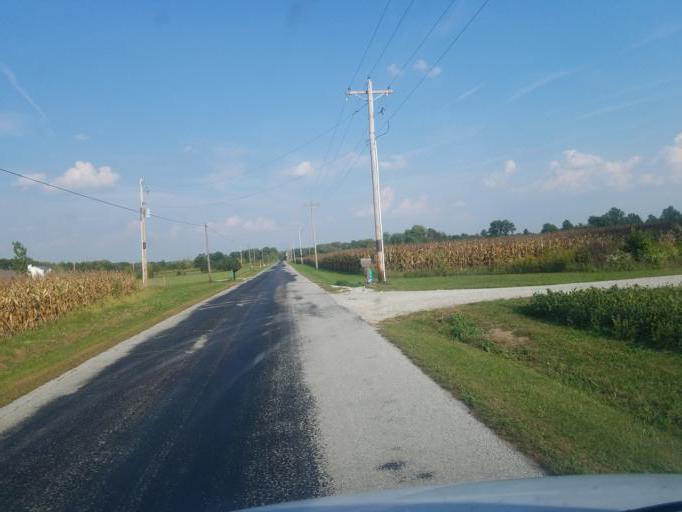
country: US
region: Ohio
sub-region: Wyandot County
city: Carey
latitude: 40.9053
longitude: -83.3768
